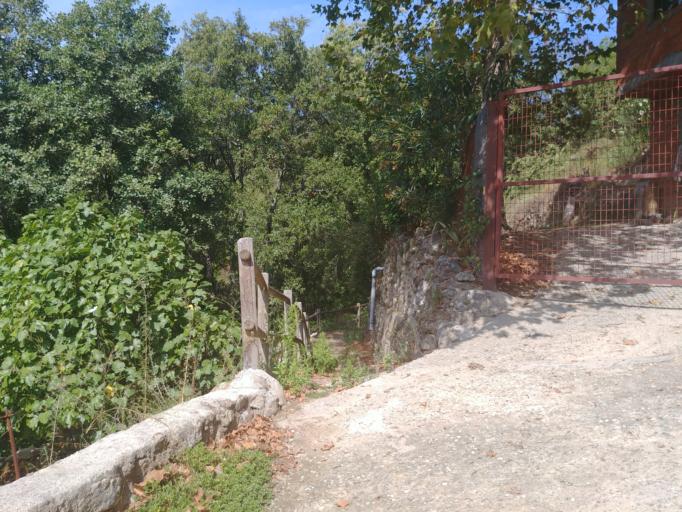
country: ES
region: Extremadura
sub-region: Provincia de Caceres
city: Garganta la Olla
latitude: 40.1138
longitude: -5.7754
